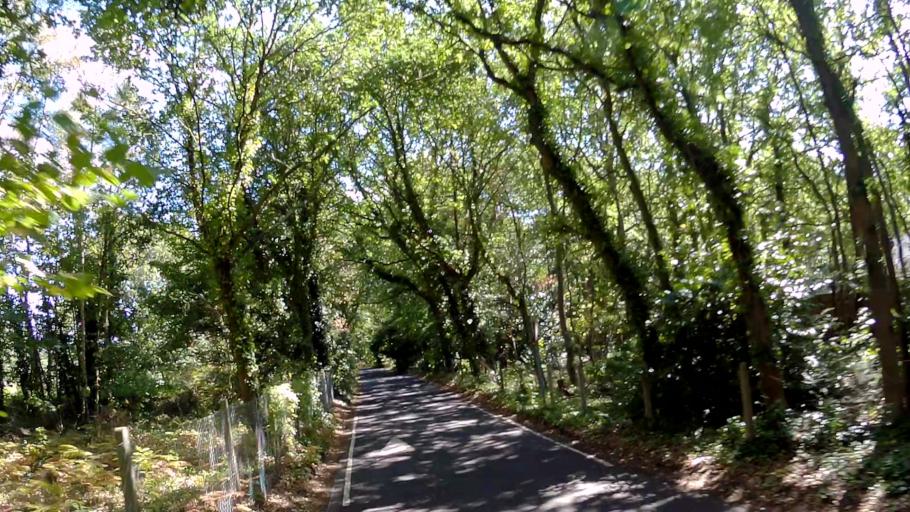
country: GB
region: England
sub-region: Bracknell Forest
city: Crowthorne
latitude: 51.3919
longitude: -0.7945
